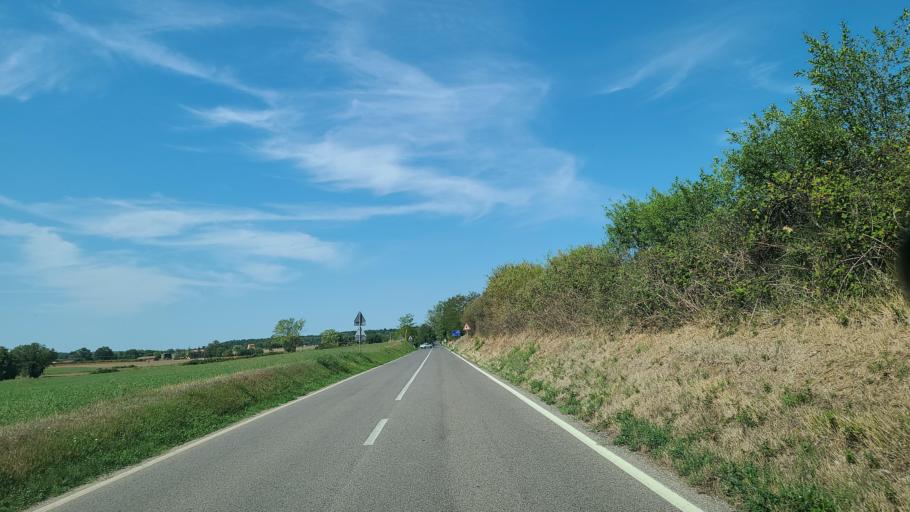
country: IT
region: Tuscany
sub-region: Provincia di Siena
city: Castellina Scalo
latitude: 43.3930
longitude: 11.2030
